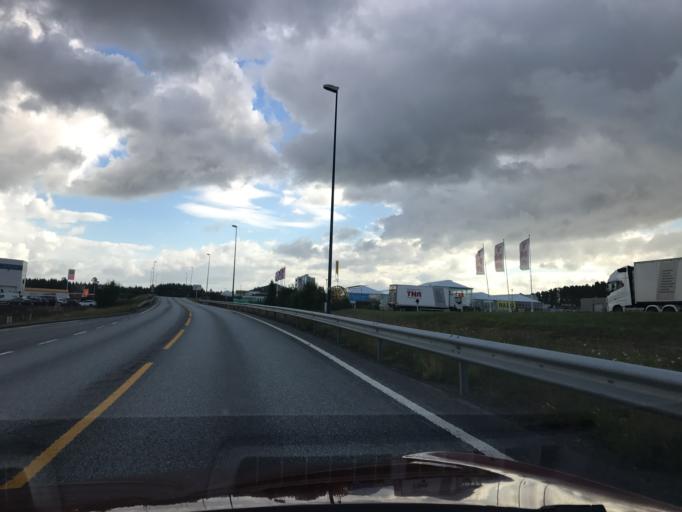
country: NO
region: Hordaland
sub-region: Stord
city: Leirvik
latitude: 59.7603
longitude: 5.4477
